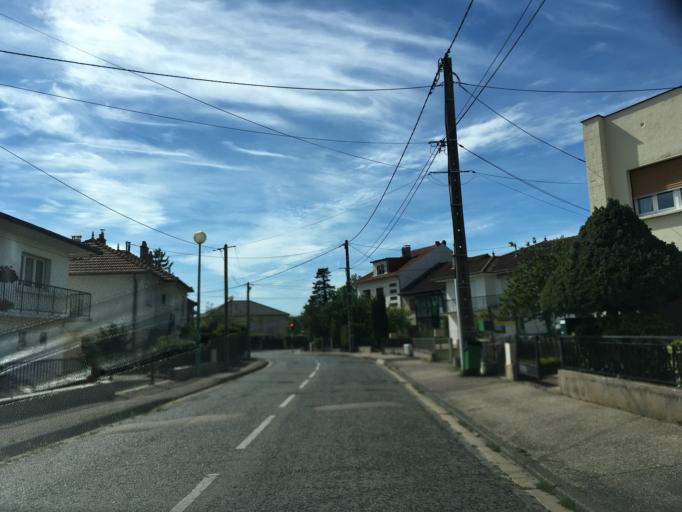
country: FR
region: Lorraine
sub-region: Departement de la Moselle
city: Marly
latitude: 49.0753
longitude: 6.1853
